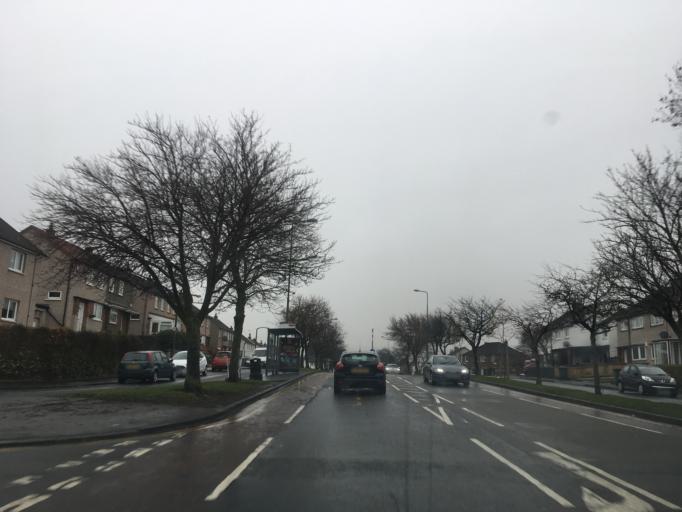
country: GB
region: Scotland
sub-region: Edinburgh
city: Currie
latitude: 55.9379
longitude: -3.2921
